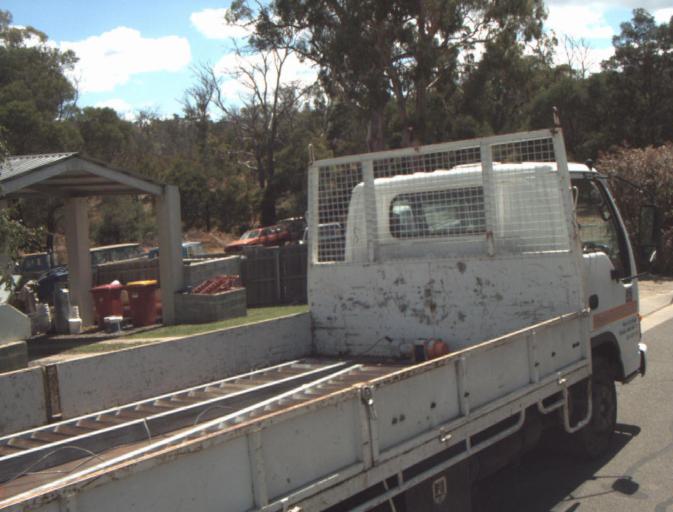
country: AU
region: Tasmania
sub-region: Launceston
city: Newstead
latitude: -41.4067
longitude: 147.1682
